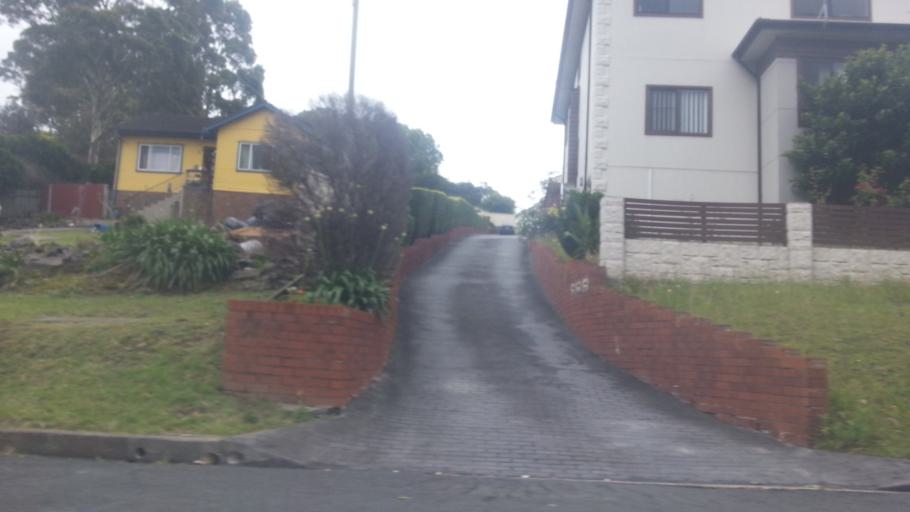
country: AU
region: New South Wales
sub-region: Wollongong
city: Mangerton
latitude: -34.4392
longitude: 150.8815
